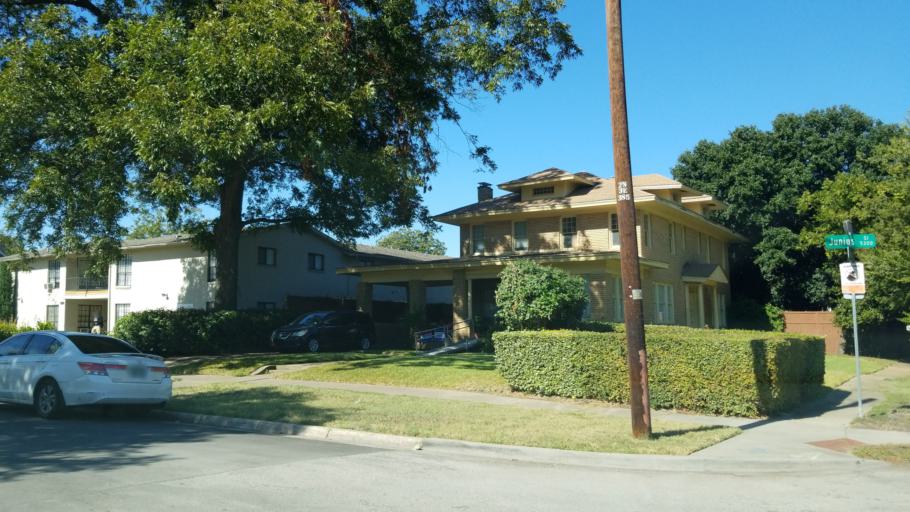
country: US
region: Texas
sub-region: Dallas County
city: Highland Park
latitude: 32.8032
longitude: -96.7635
